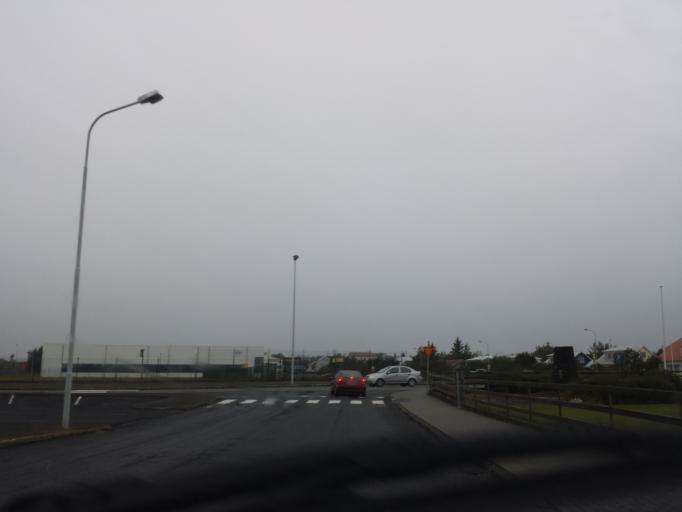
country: IS
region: Southern Peninsula
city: Reykjanesbaer
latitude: 63.9994
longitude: -22.5569
